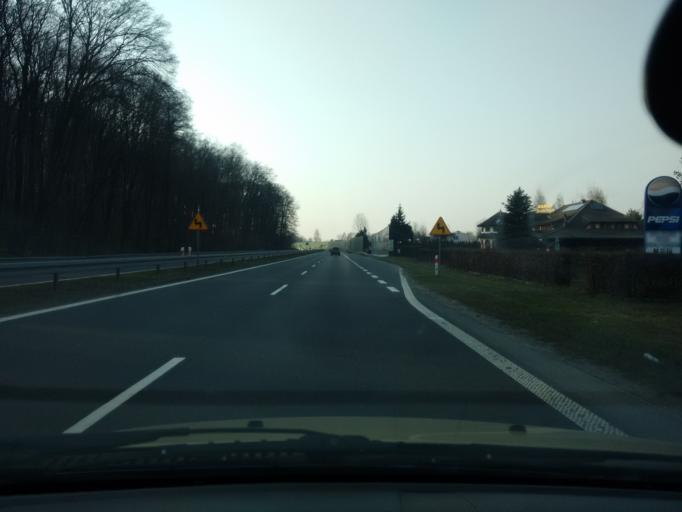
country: PL
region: Silesian Voivodeship
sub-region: Powiat cieszynski
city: Ochaby
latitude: 49.8320
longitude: 18.7858
